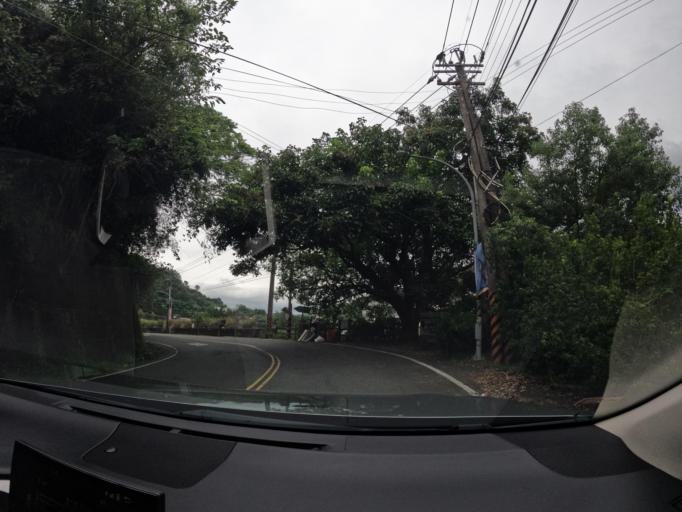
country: TW
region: Taiwan
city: Fengyuan
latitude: 24.3377
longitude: 120.8742
